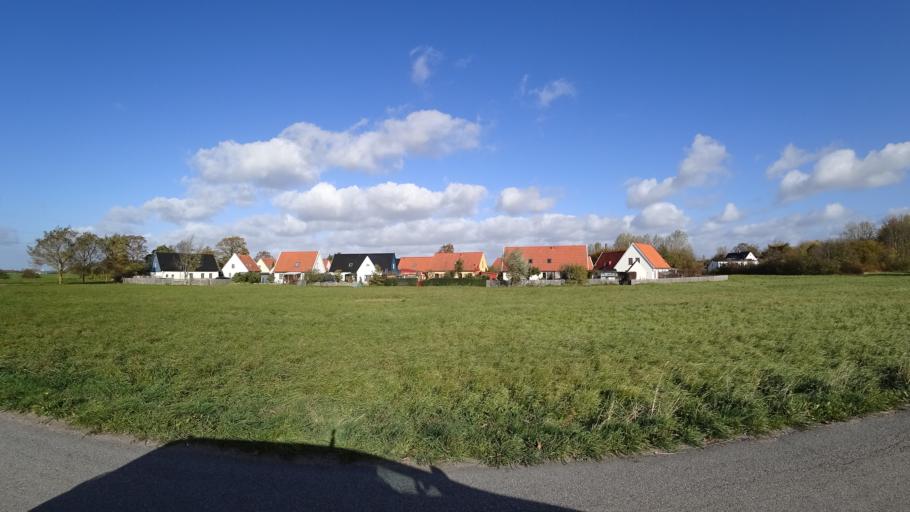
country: SE
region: Skane
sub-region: Staffanstorps Kommun
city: Hjaerup
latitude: 55.6822
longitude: 13.1645
